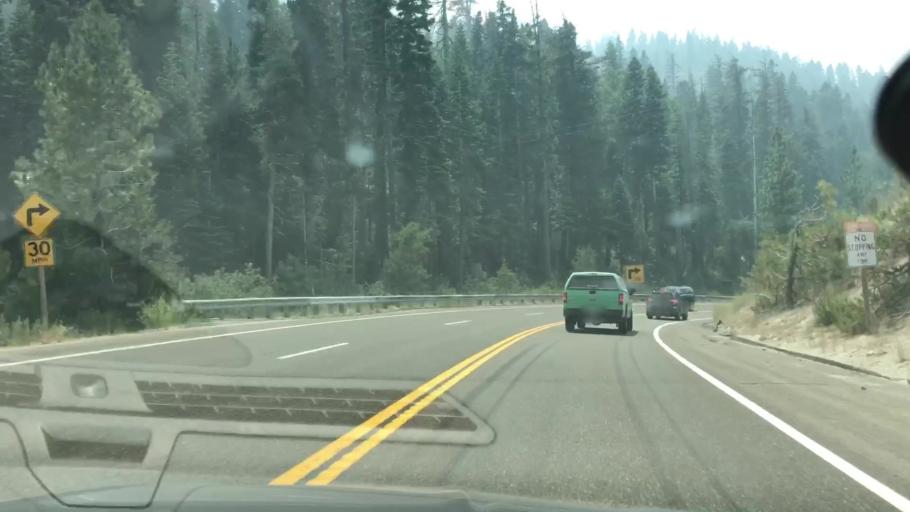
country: US
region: California
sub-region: El Dorado County
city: South Lake Tahoe
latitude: 38.8023
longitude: -120.1194
